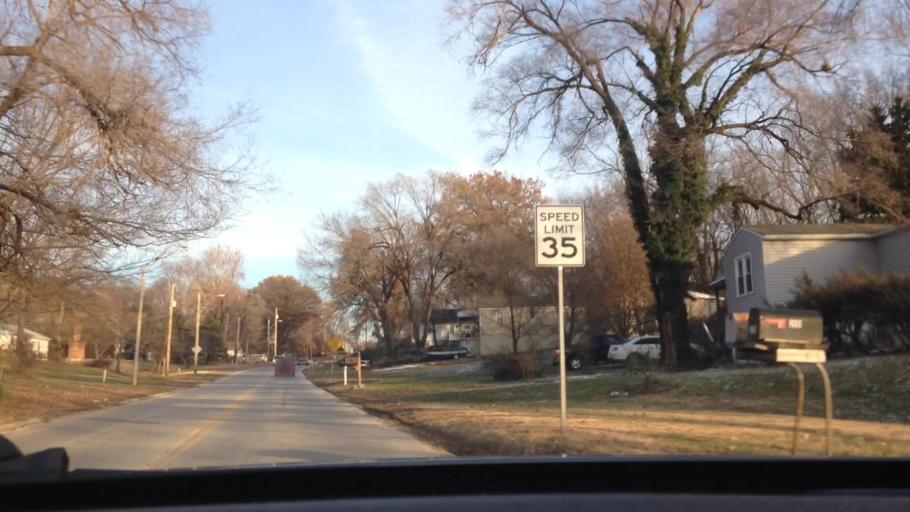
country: US
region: Missouri
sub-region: Clay County
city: North Kansas City
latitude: 39.1632
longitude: -94.5467
